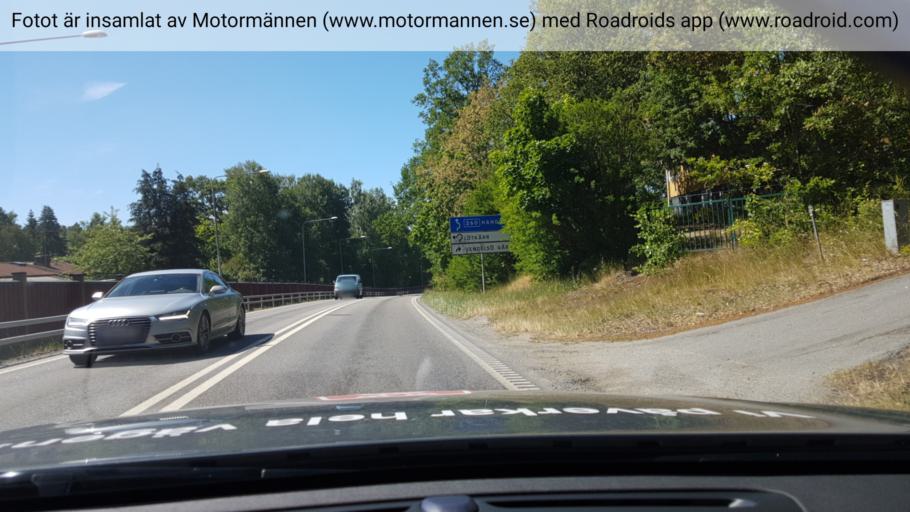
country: SE
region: Stockholm
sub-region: Tyreso Kommun
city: Bollmora
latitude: 59.2060
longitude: 18.2047
